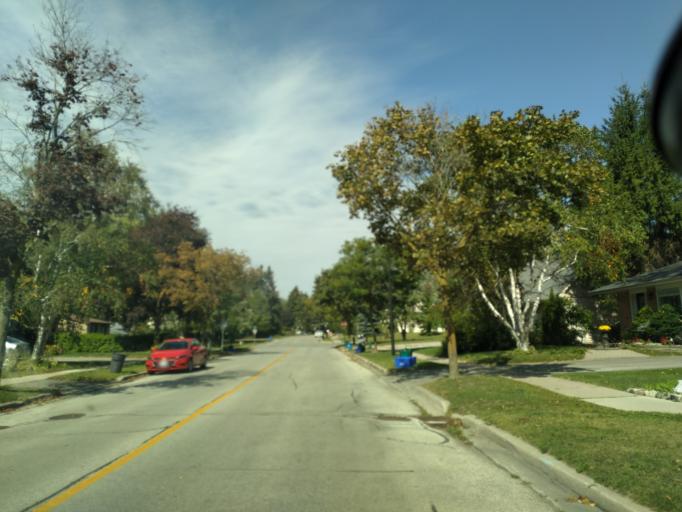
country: CA
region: Ontario
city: Newmarket
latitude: 44.0710
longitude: -79.4422
